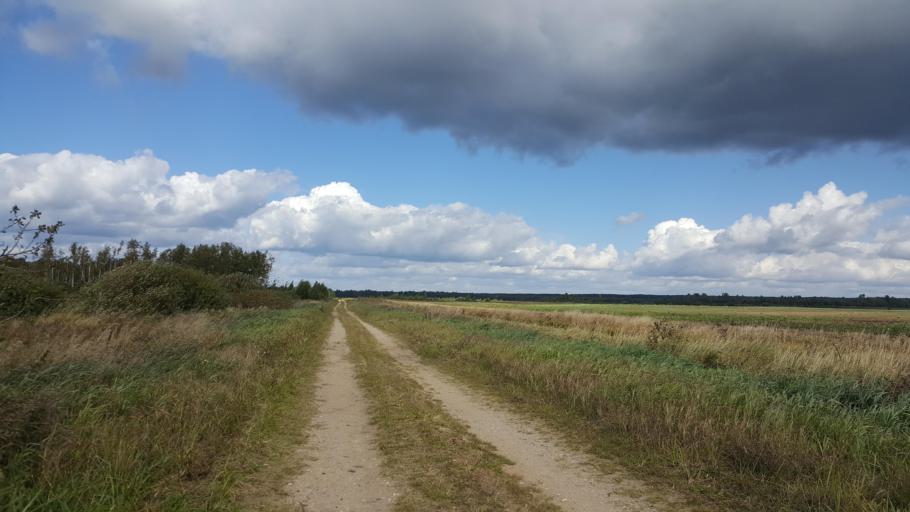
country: BY
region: Brest
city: Kamyanyets
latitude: 52.4503
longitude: 23.9345
